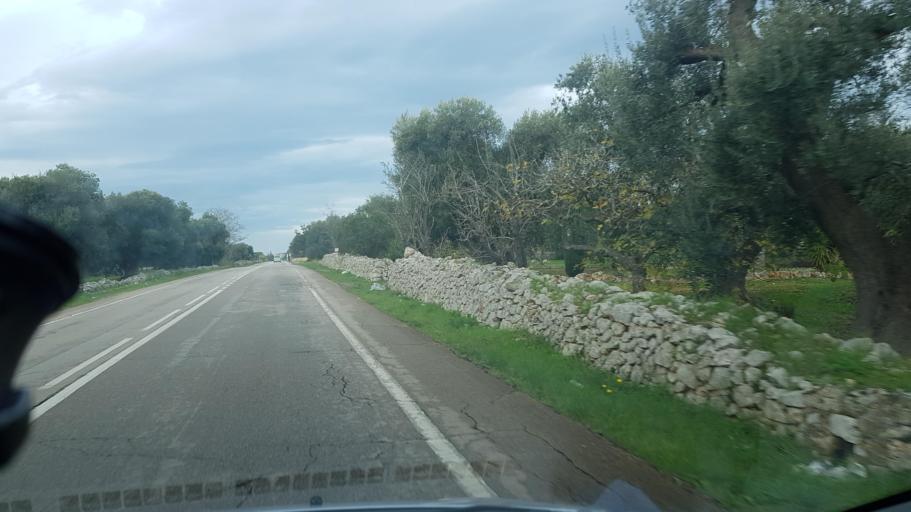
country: IT
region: Apulia
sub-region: Provincia di Brindisi
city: San Vito dei Normanni
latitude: 40.6736
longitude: 17.6910
